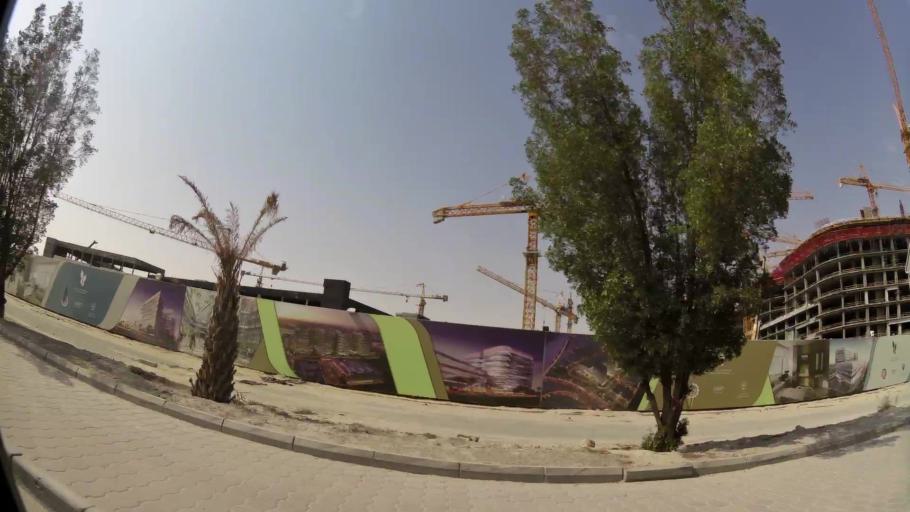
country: KW
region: Muhafazat al Jahra'
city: Al Jahra'
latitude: 29.3361
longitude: 47.6839
